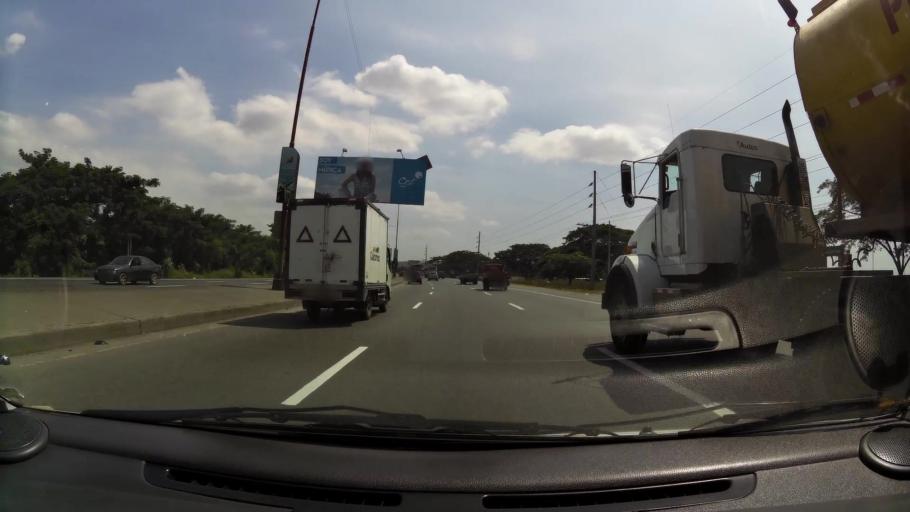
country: EC
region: Guayas
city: Eloy Alfaro
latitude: -2.0507
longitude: -79.8854
